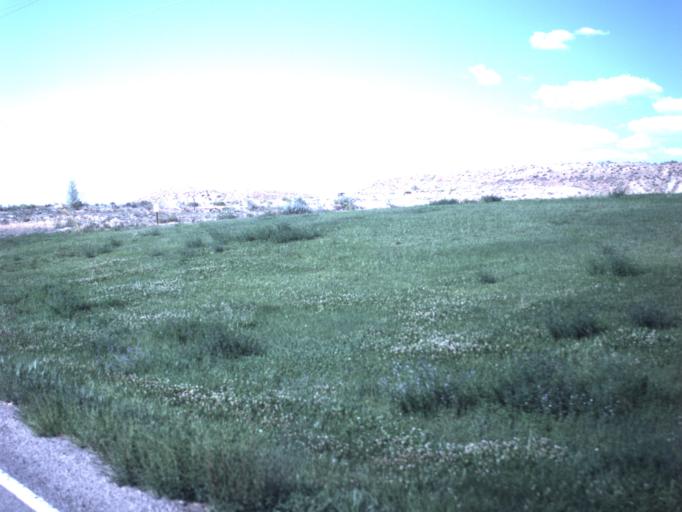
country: US
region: Utah
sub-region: Emery County
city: Huntington
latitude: 39.3632
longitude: -110.8520
